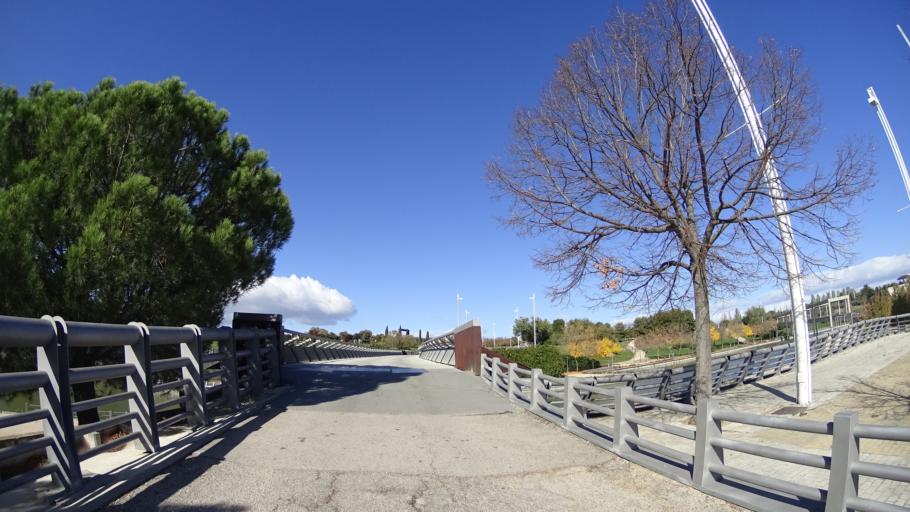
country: ES
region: Madrid
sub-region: Provincia de Madrid
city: San Blas
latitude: 40.4586
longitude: -3.6082
